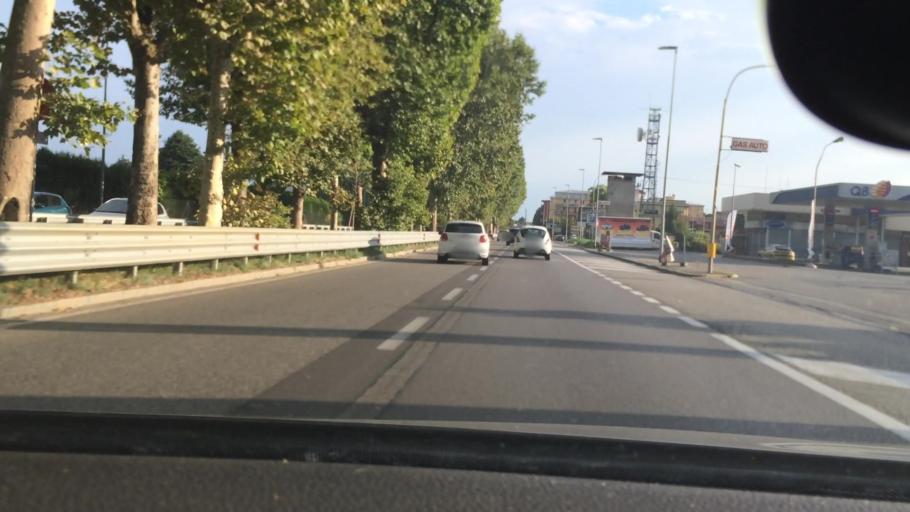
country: IT
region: Lombardy
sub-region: Provincia di Bergamo
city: Gorle
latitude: 45.6984
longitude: 9.6951
